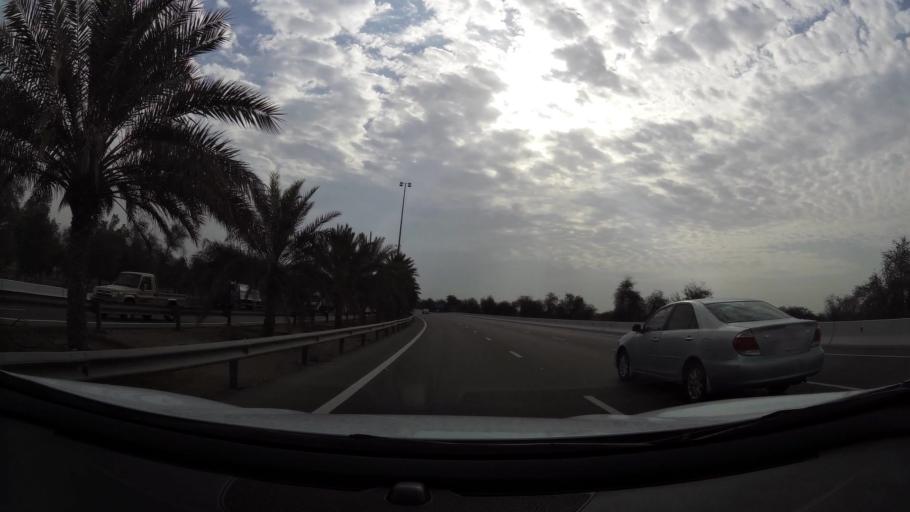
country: AE
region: Abu Dhabi
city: Al Ain
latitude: 24.2022
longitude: 55.5694
